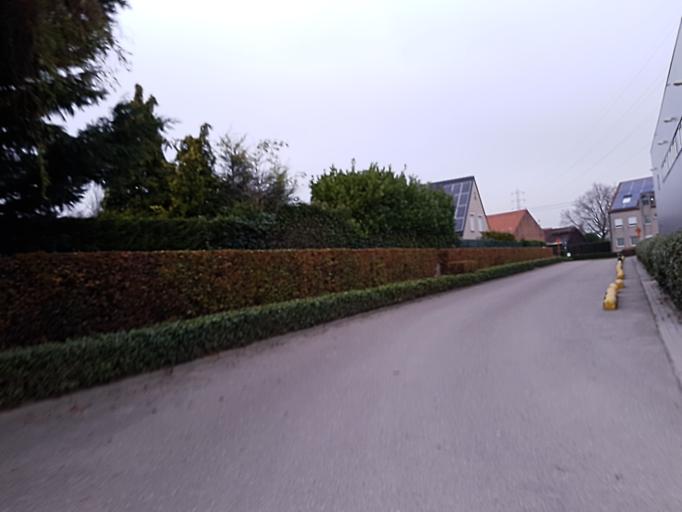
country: BE
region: Flanders
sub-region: Provincie Antwerpen
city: Rumst
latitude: 51.0314
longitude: 4.4103
